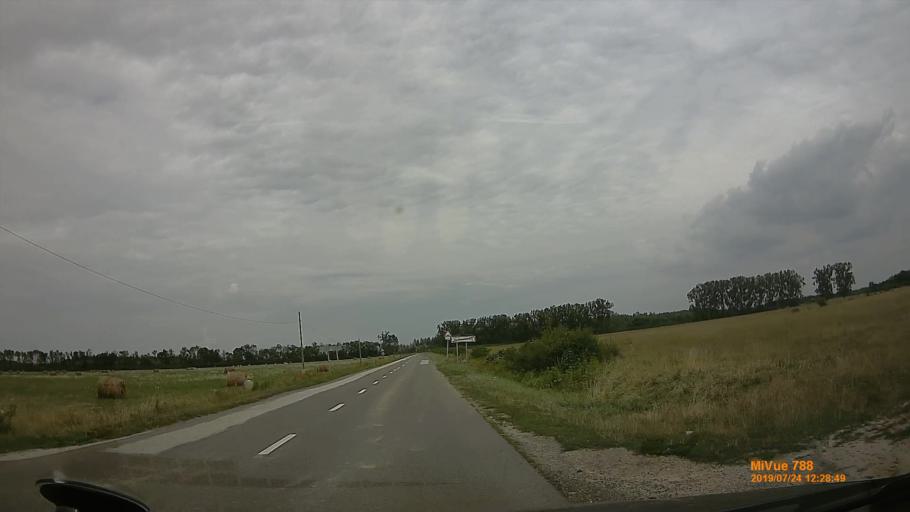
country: HU
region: Szabolcs-Szatmar-Bereg
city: Vasarosnameny
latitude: 48.1448
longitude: 22.3453
